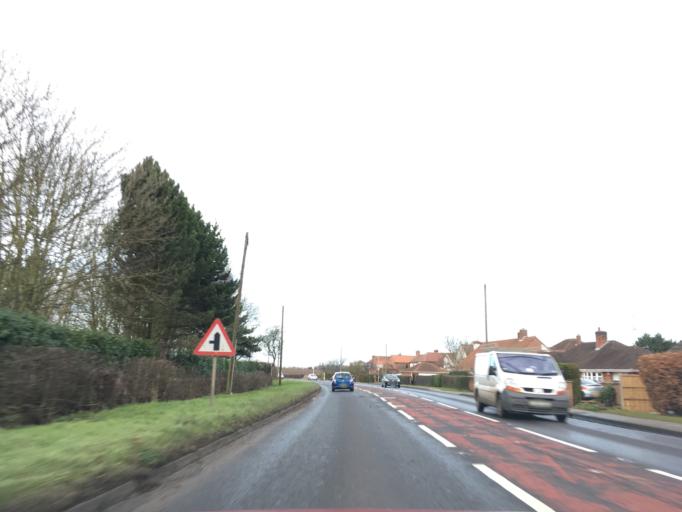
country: GB
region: England
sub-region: Nottinghamshire
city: Ruddington
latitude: 52.8764
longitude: -1.1318
